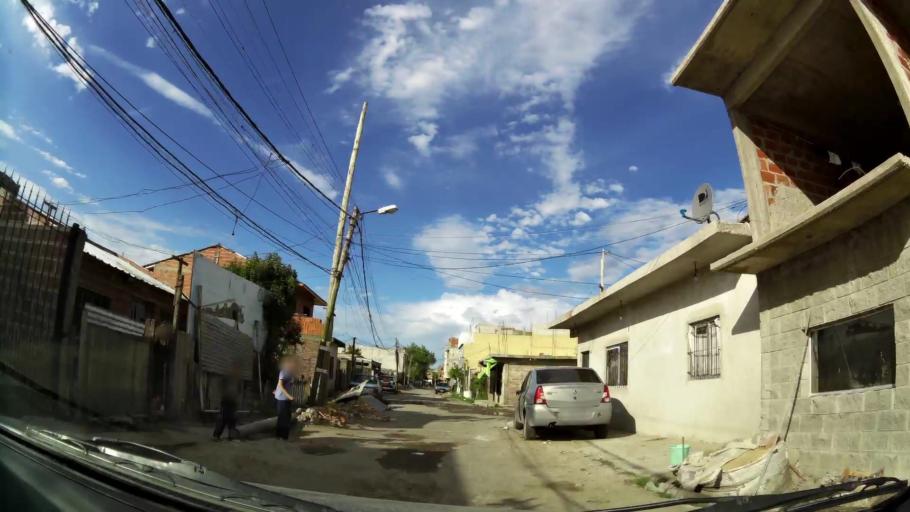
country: AR
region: Buenos Aires
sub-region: Partido de Lanus
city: Lanus
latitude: -34.7028
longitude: -58.3600
